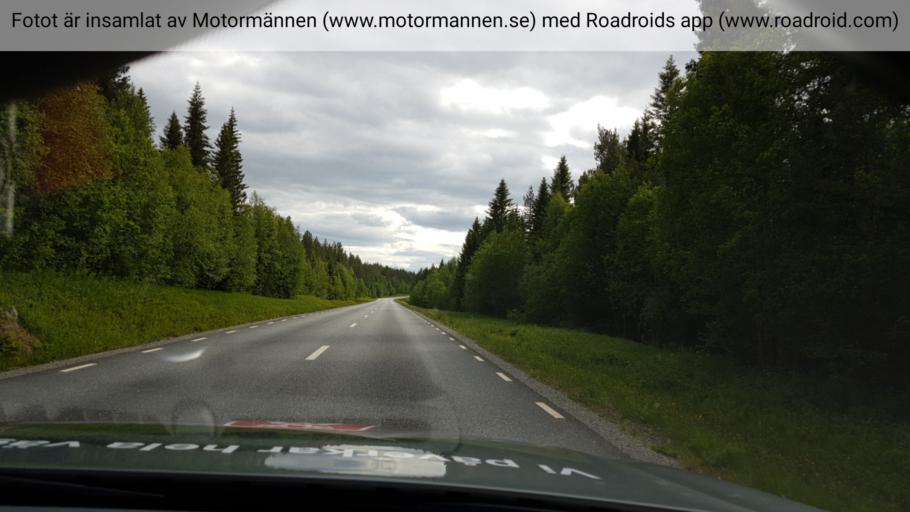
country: SE
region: Jaemtland
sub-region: Stroemsunds Kommun
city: Stroemsund
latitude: 63.9974
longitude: 15.5124
